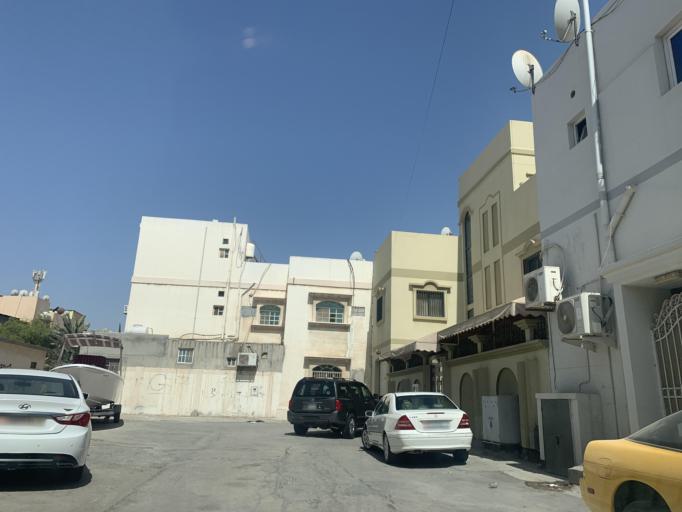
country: BH
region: Manama
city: Jidd Hafs
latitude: 26.2266
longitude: 50.5377
